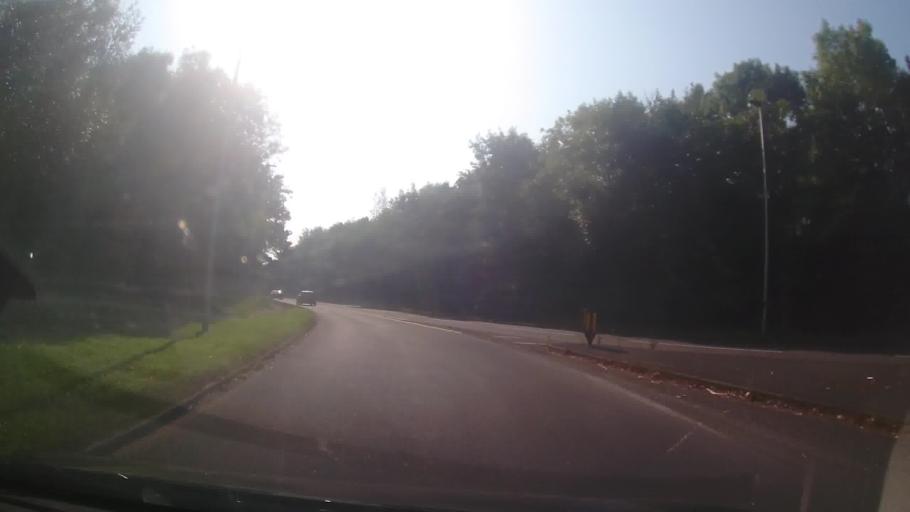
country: GB
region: England
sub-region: Shropshire
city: Bridgnorth
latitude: 52.5322
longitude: -2.4368
